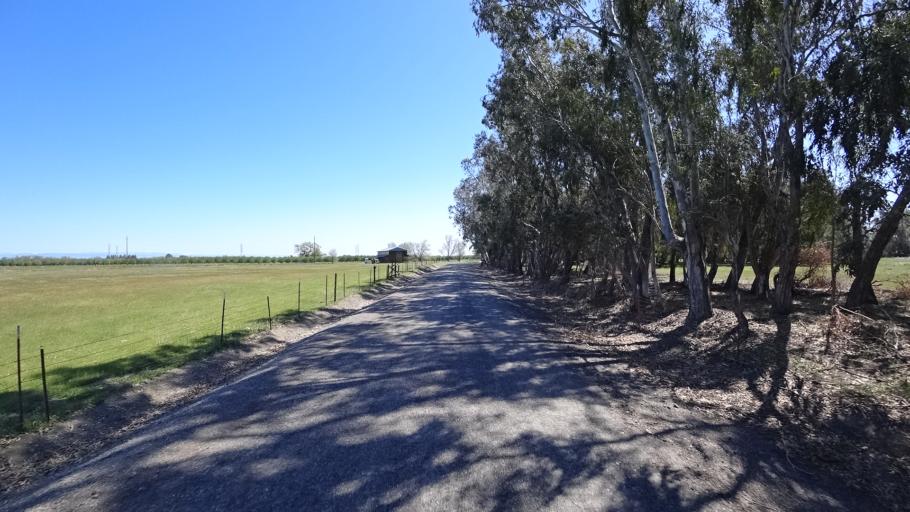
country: US
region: California
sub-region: Glenn County
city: Orland
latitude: 39.7854
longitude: -122.2736
